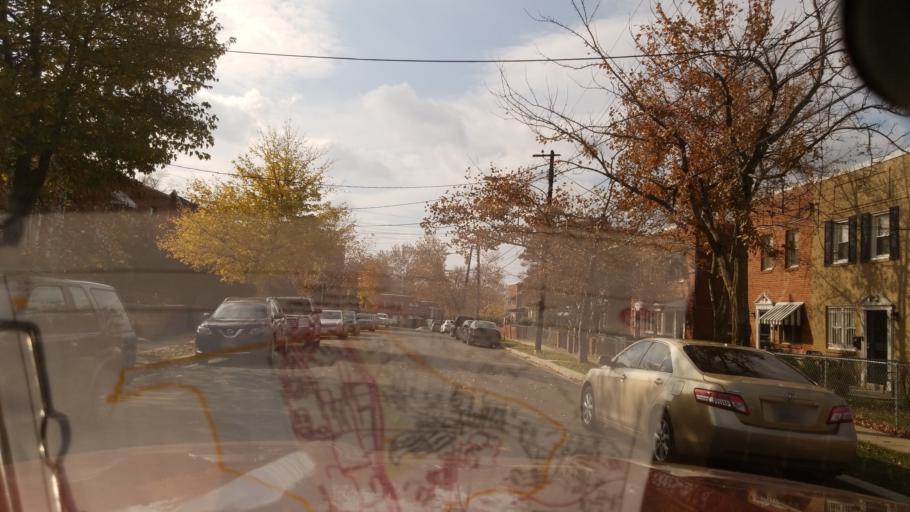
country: US
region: Maryland
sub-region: Prince George's County
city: Glassmanor
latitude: 38.8337
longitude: -76.9978
